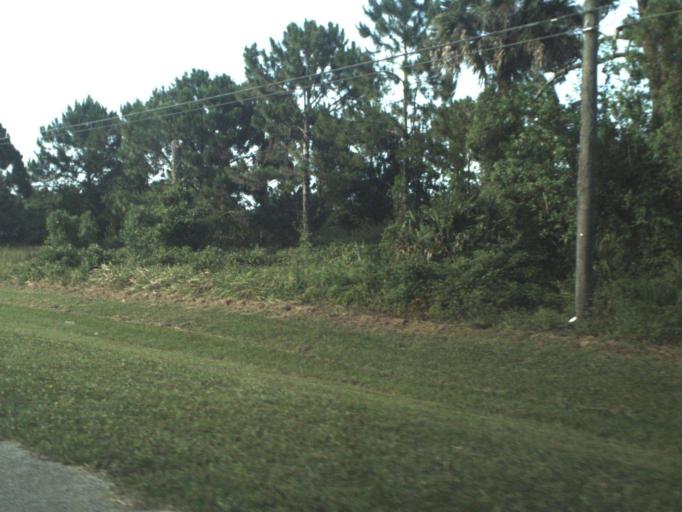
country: US
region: Florida
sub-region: Volusia County
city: Oak Hill
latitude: 28.9233
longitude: -80.8731
